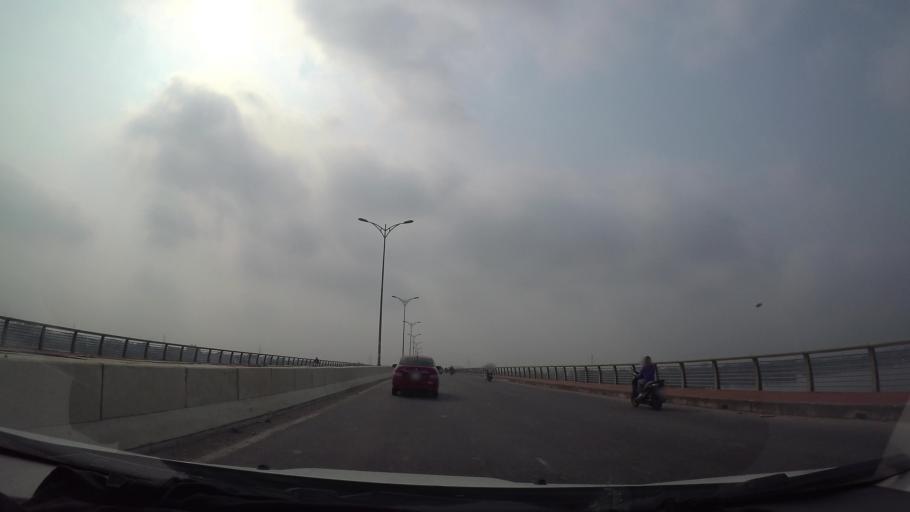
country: VN
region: Da Nang
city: Cam Le
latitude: 16.0160
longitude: 108.2138
